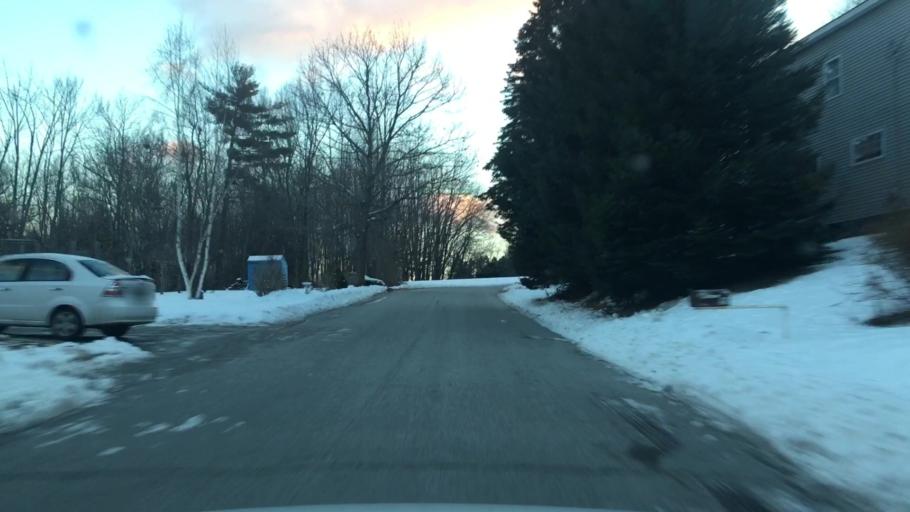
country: US
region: Maine
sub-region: Androscoggin County
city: Auburn
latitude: 44.0804
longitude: -70.2499
